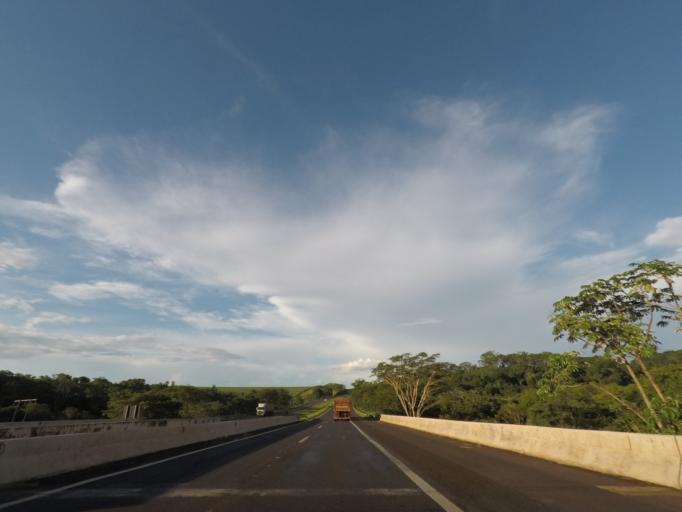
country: BR
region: Sao Paulo
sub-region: Ituverava
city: Ituverava
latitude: -20.2566
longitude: -47.7998
